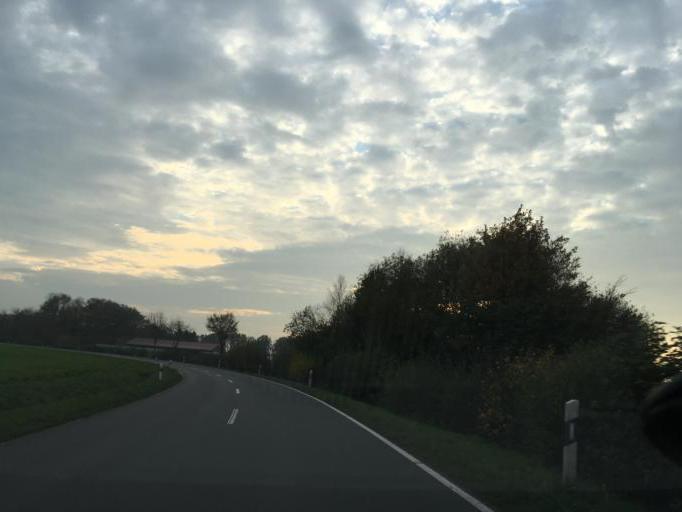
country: DE
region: Lower Saxony
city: Bergen
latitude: 52.8324
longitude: 9.9707
